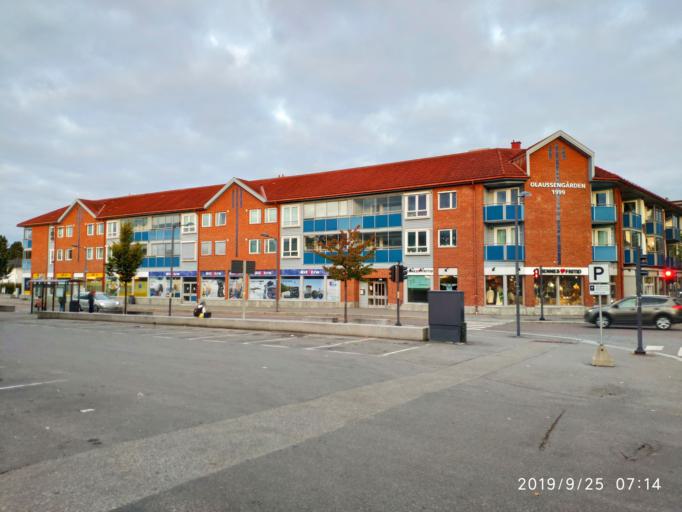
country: NO
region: Akershus
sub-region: Skedsmo
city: Lillestrom
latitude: 59.9456
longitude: 11.0074
